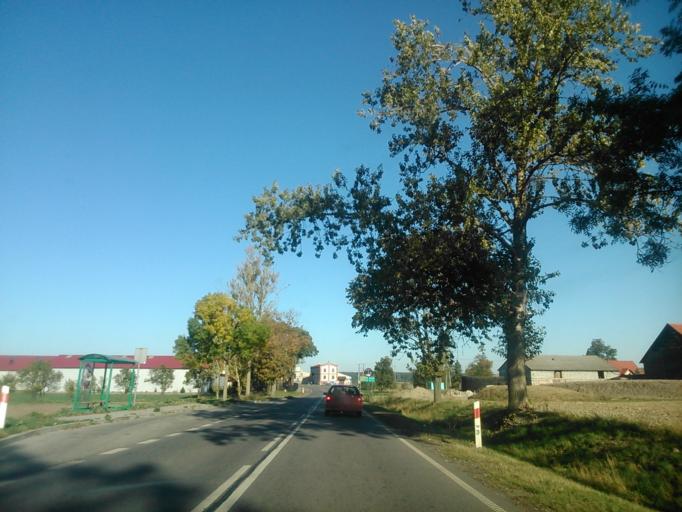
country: PL
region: Kujawsko-Pomorskie
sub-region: Powiat wabrzeski
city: Debowa Laka
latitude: 53.2491
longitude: 19.0291
